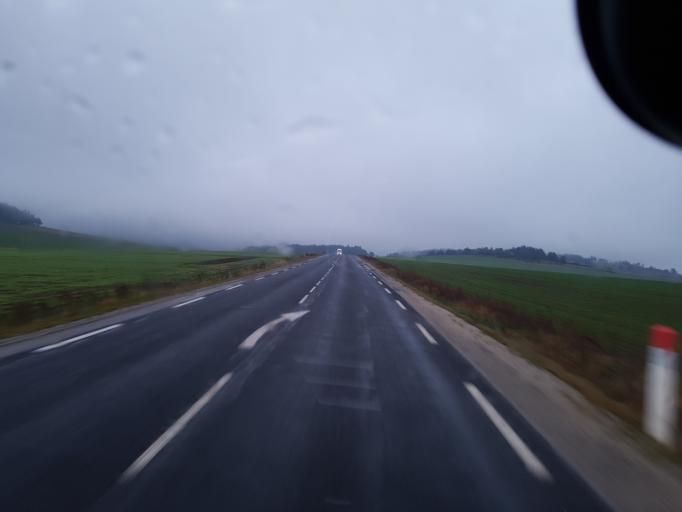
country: FR
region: Languedoc-Roussillon
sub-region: Departement de la Lozere
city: Langogne
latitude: 44.8353
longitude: 3.8608
